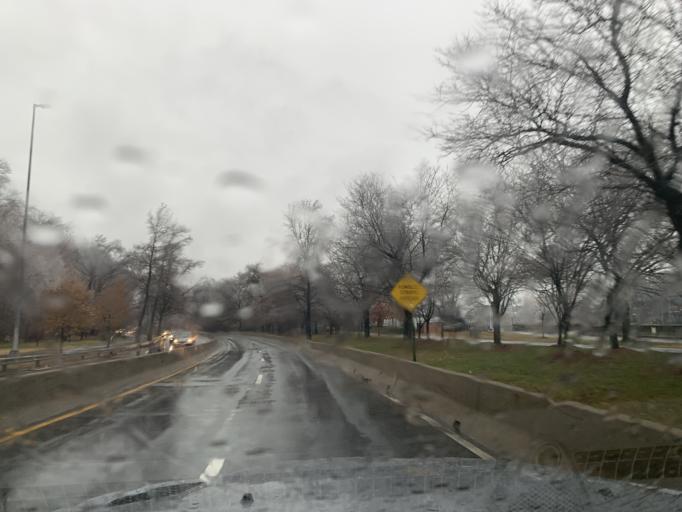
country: US
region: New York
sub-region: New York County
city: Inwood
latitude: 40.8550
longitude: -73.9233
